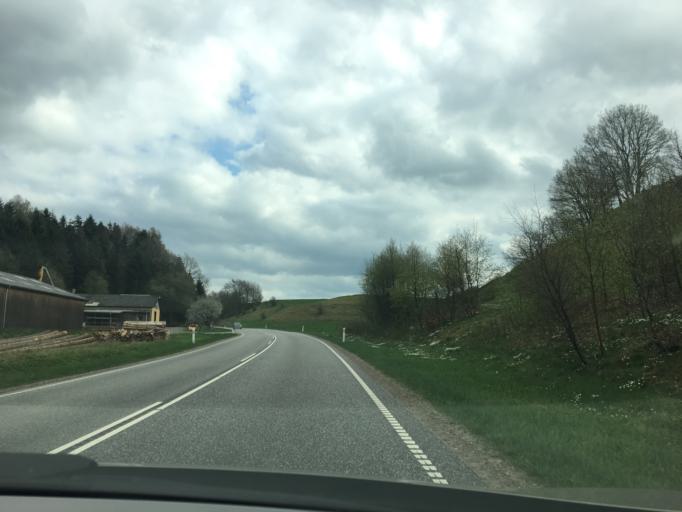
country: DK
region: Central Jutland
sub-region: Horsens Kommune
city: Braedstrup
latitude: 56.0398
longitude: 9.5992
